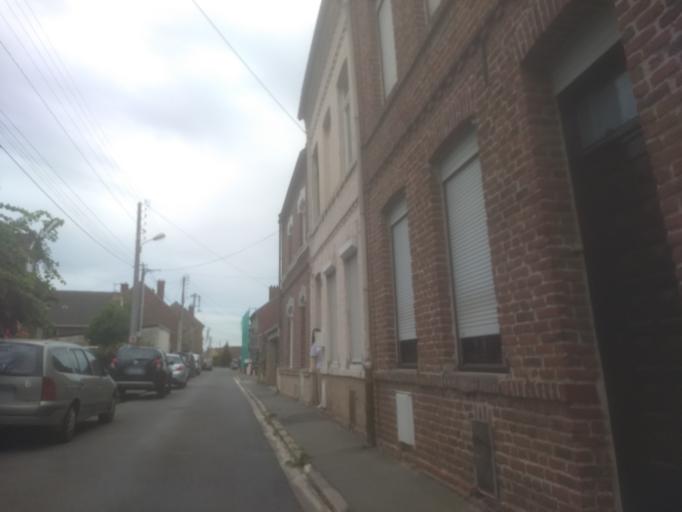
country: FR
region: Nord-Pas-de-Calais
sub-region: Departement du Pas-de-Calais
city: Arras
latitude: 50.2795
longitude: 2.7741
